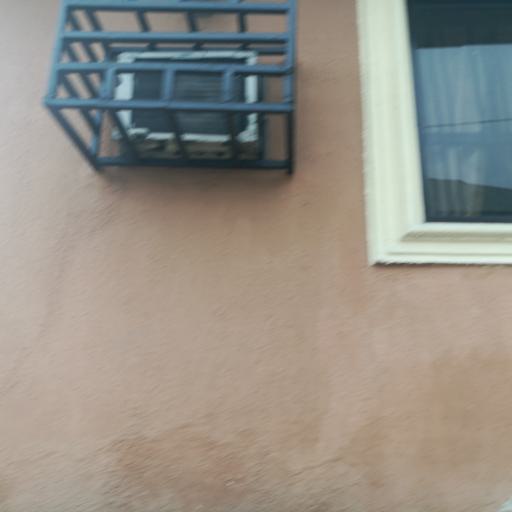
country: NG
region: Rivers
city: Port Harcourt
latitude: 4.7525
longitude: 7.0095
